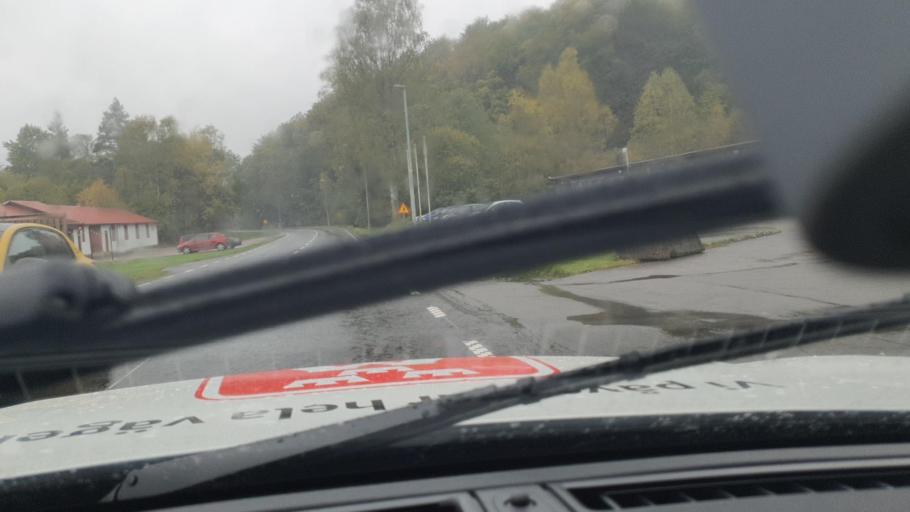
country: SE
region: Vaestra Goetaland
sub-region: Marks Kommun
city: Horred
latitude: 57.1626
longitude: 12.7448
